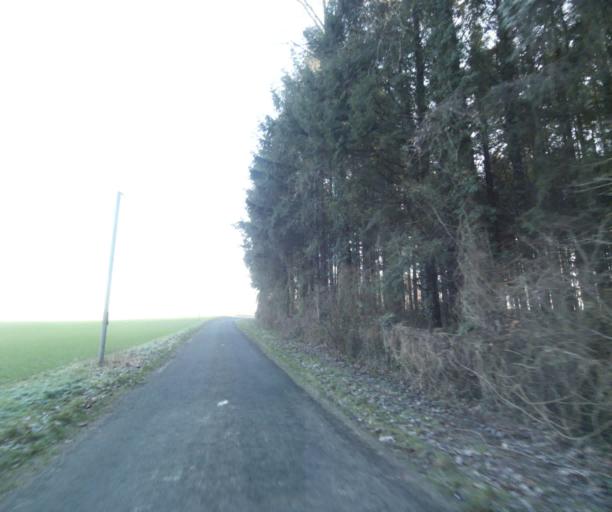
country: FR
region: Champagne-Ardenne
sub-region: Departement de la Haute-Marne
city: Bienville
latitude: 48.4981
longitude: 5.0561
